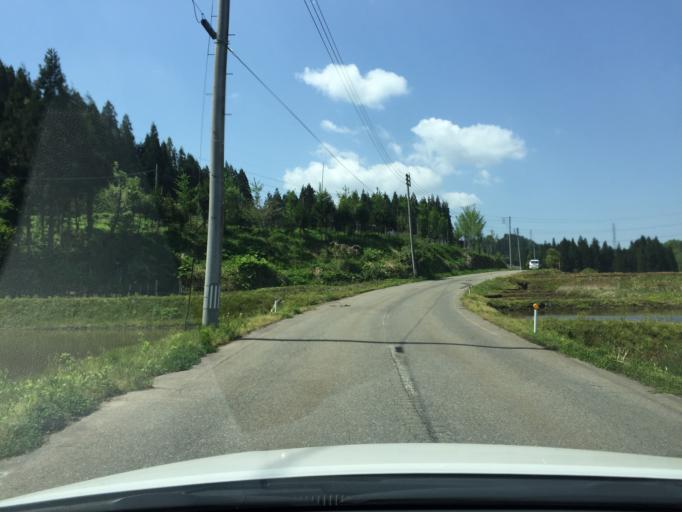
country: JP
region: Niigata
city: Tochio-honcho
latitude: 37.4856
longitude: 139.0508
